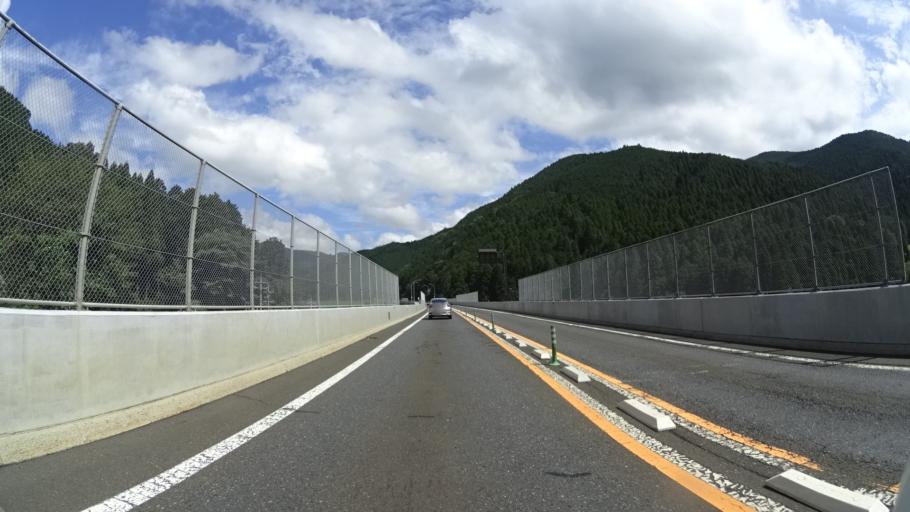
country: JP
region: Hyogo
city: Yamazakicho-nakabirose
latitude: 35.1935
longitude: 134.3352
